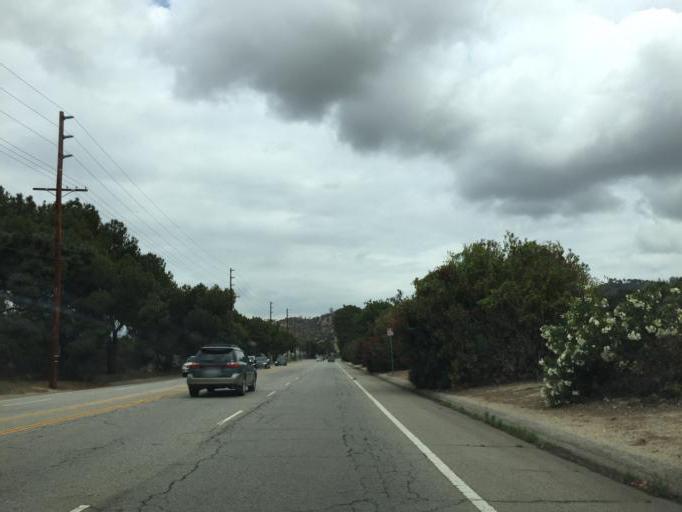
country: US
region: California
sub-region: Los Angeles County
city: Burbank
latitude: 34.1528
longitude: -118.3224
